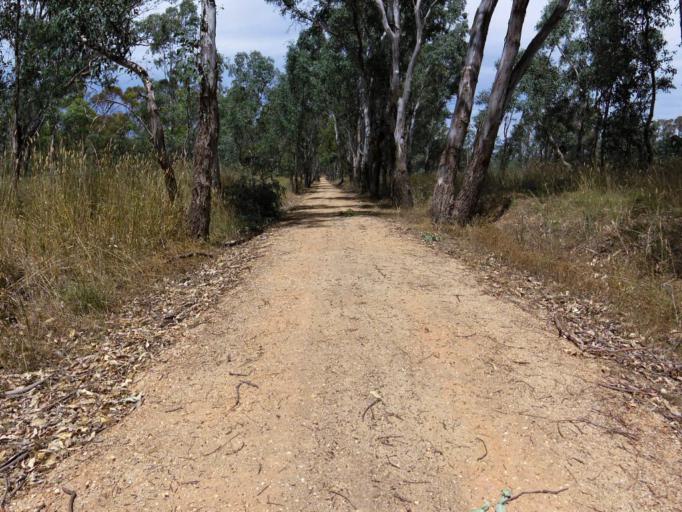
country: AU
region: Victoria
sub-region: Greater Bendigo
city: Kennington
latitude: -36.8814
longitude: 144.6482
